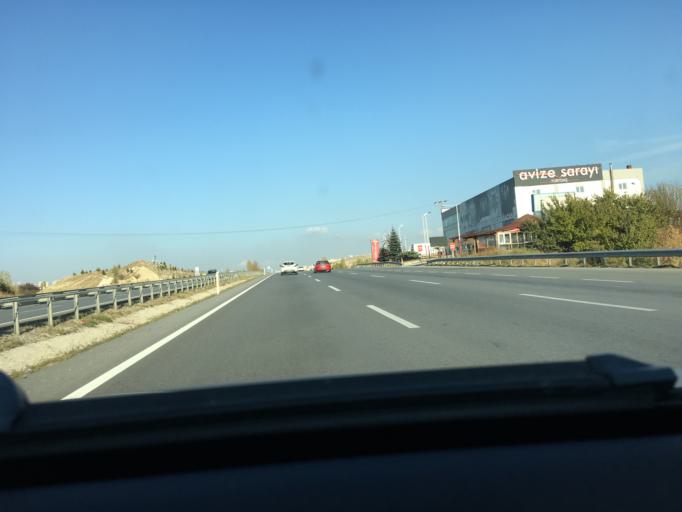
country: TR
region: Ankara
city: Temelli
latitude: 39.7868
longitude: 32.5186
